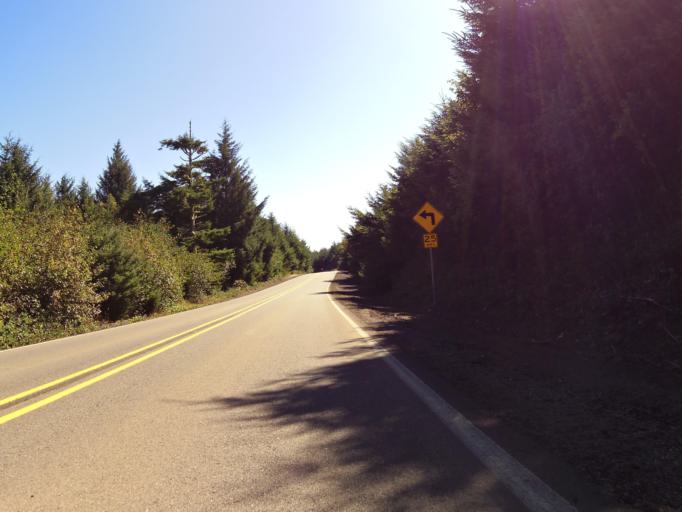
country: US
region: Oregon
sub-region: Coos County
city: Barview
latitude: 43.2722
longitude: -124.3546
